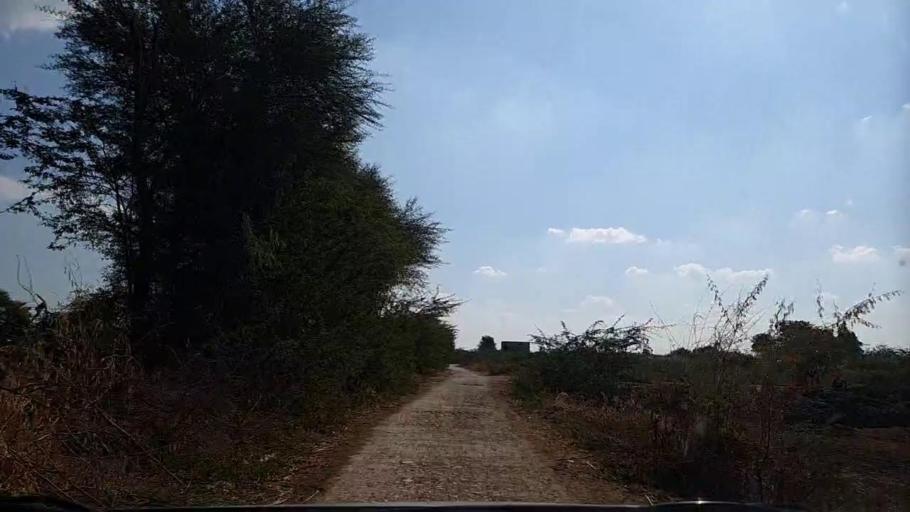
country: PK
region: Sindh
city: Pithoro
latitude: 25.6418
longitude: 69.4475
